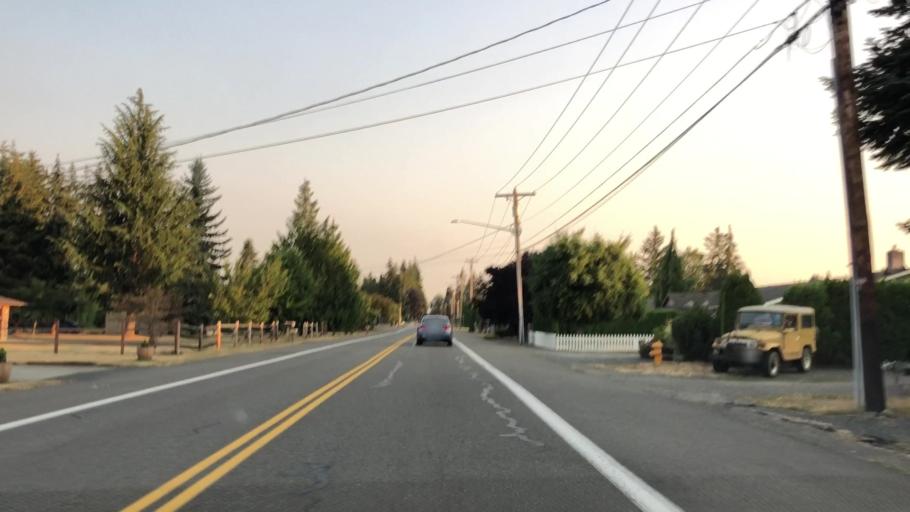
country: US
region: Washington
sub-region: Snohomish County
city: Marysville
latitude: 48.0811
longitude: -122.1622
